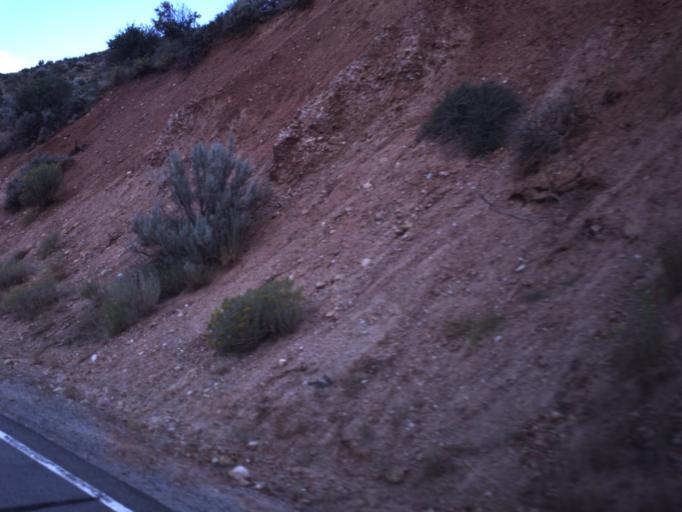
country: US
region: Utah
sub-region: Rich County
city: Randolph
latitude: 41.8106
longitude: -111.2622
